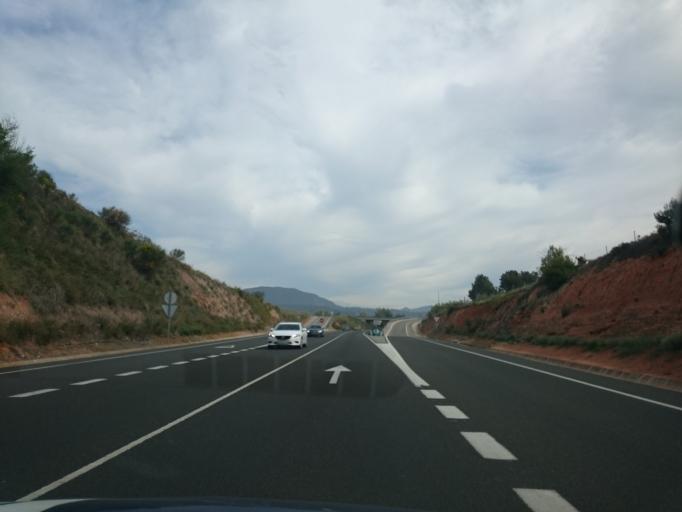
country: ES
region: Catalonia
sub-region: Provincia de Barcelona
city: Sant Pere de Riudebitlles
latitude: 41.4763
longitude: 1.6953
